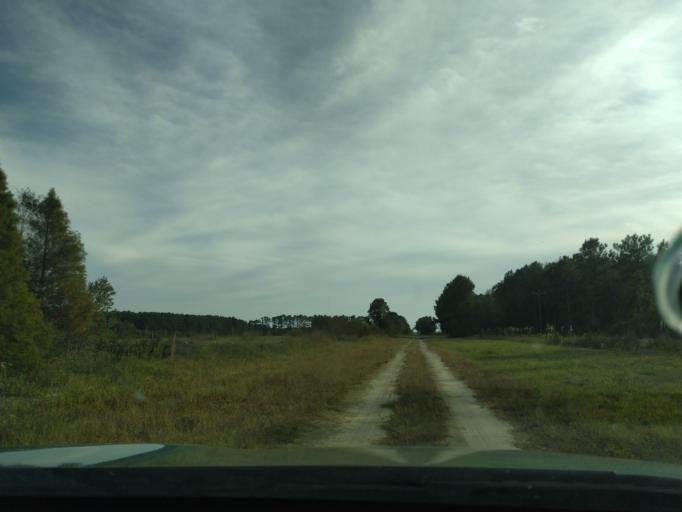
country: US
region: North Carolina
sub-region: Beaufort County
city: Belhaven
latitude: 35.6681
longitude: -76.5482
